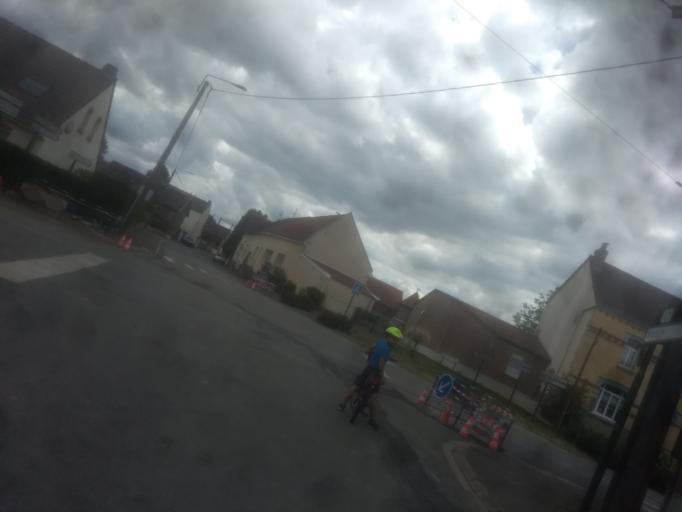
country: FR
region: Nord-Pas-de-Calais
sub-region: Departement du Pas-de-Calais
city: Agny
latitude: 50.2278
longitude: 2.7390
